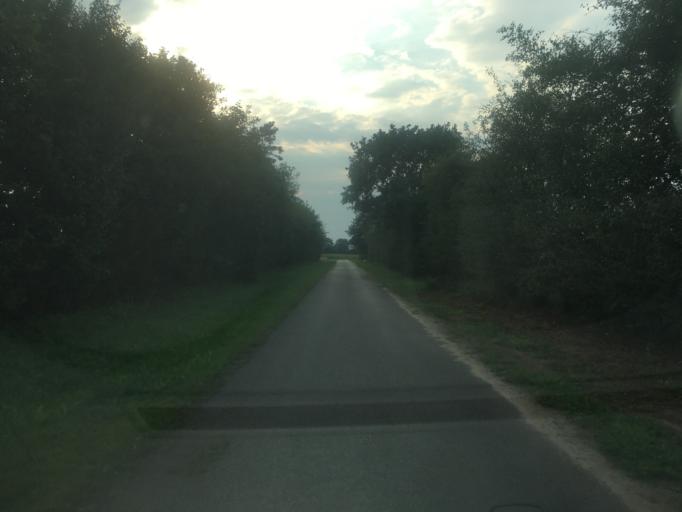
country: DK
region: South Denmark
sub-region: Tonder Kommune
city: Logumkloster
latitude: 55.0415
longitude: 8.9179
